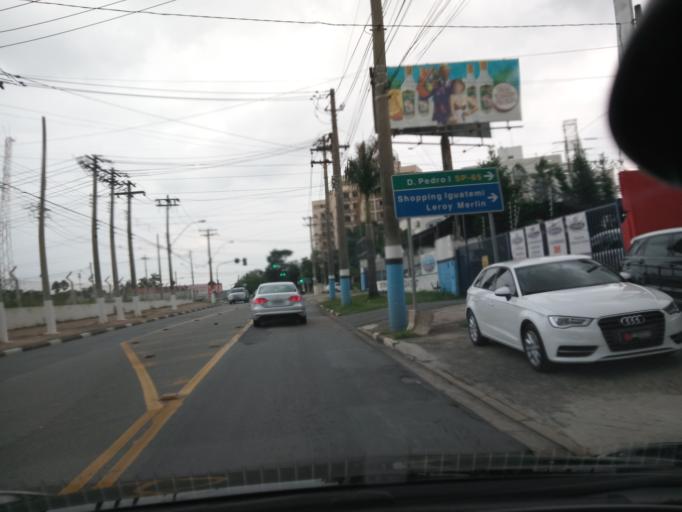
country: BR
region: Sao Paulo
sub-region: Campinas
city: Campinas
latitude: -22.8917
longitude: -47.0340
